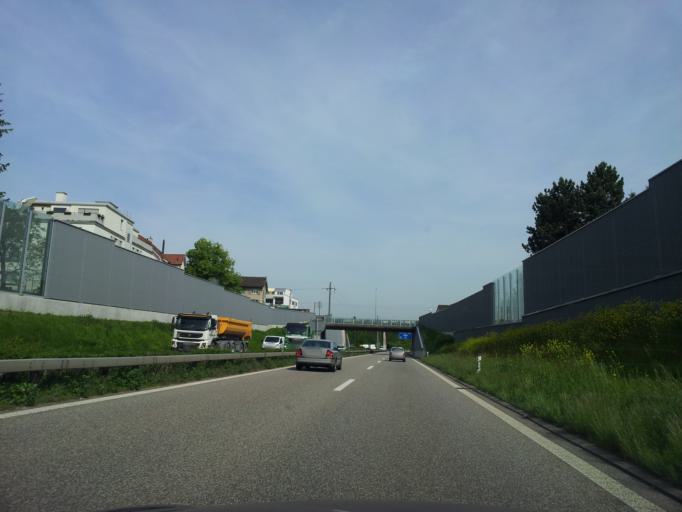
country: CH
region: Zurich
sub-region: Bezirk Buelach
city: Buelach / Niederflachs
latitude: 47.5122
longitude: 8.5271
